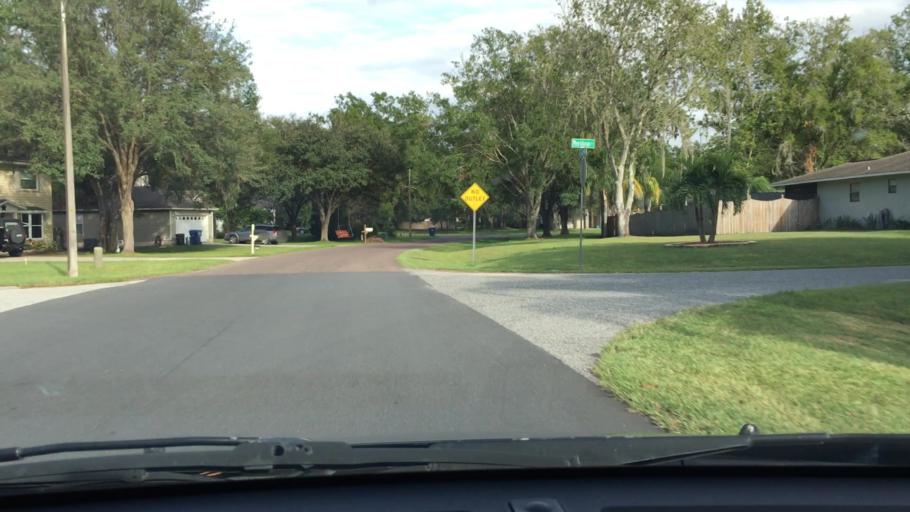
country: US
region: Florida
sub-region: Pasco County
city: Land O' Lakes
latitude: 28.2137
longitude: -82.4248
